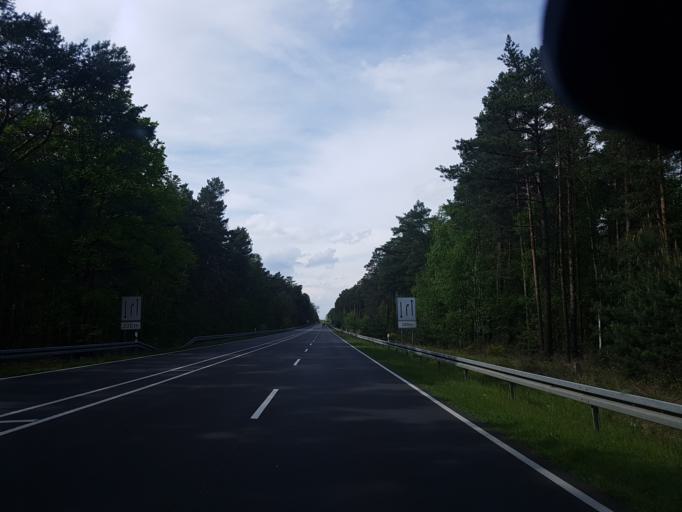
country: DE
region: Saxony
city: Gross Duben
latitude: 51.6571
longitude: 14.5319
